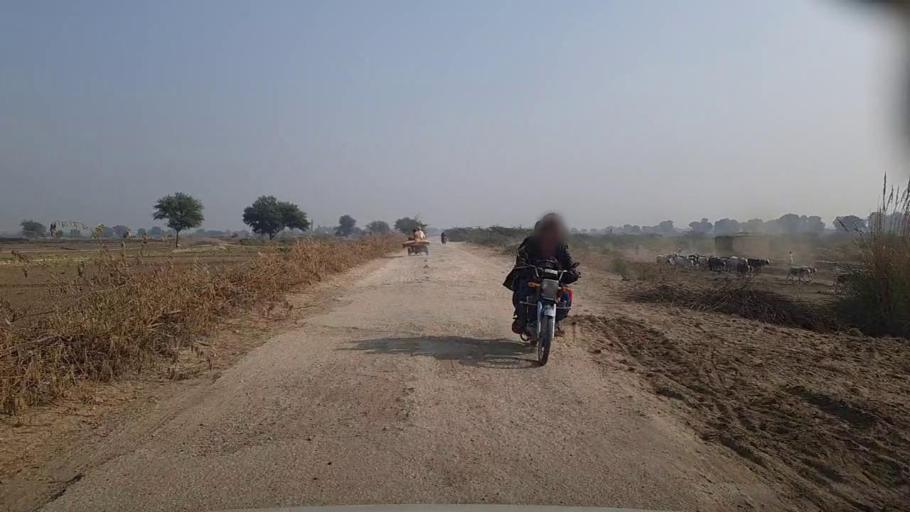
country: PK
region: Sindh
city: Setharja Old
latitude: 27.0655
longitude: 68.4520
